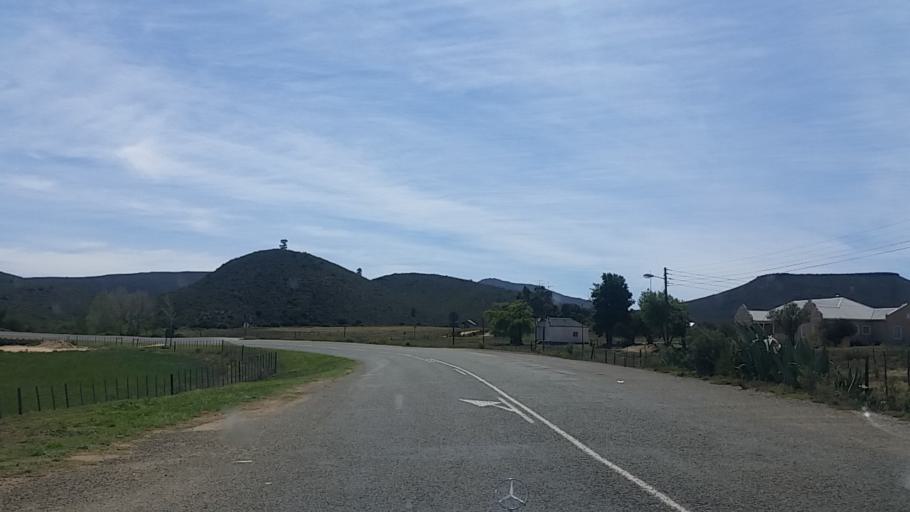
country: ZA
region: Western Cape
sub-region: Eden District Municipality
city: Knysna
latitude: -33.6445
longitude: 23.1376
